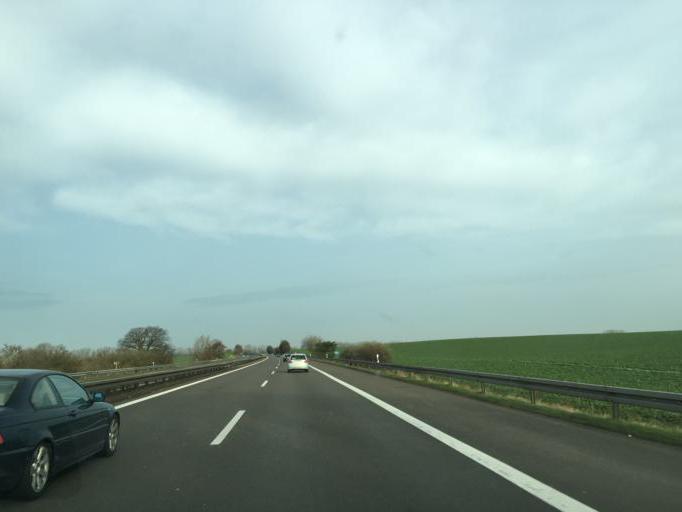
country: DE
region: Brandenburg
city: Kremmen
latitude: 52.7431
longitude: 12.9032
